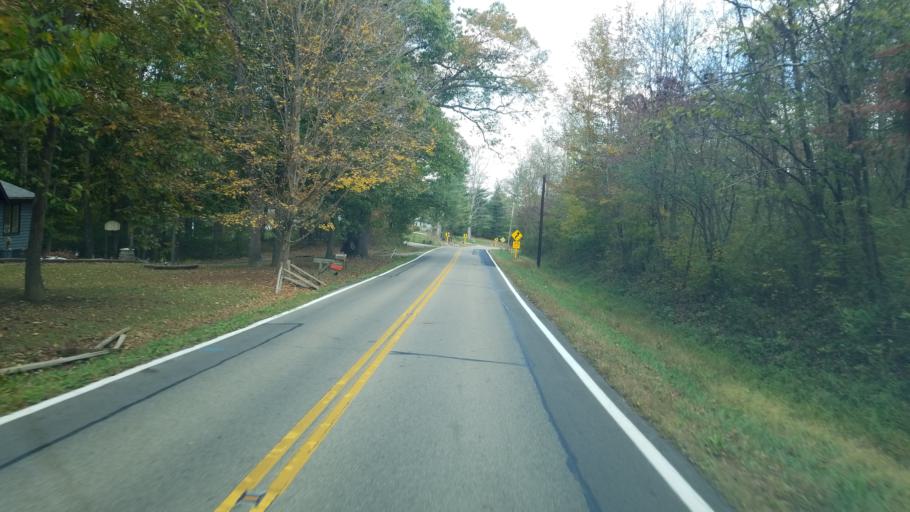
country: US
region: Ohio
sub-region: Jackson County
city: Wellston
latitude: 39.0941
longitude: -82.5815
